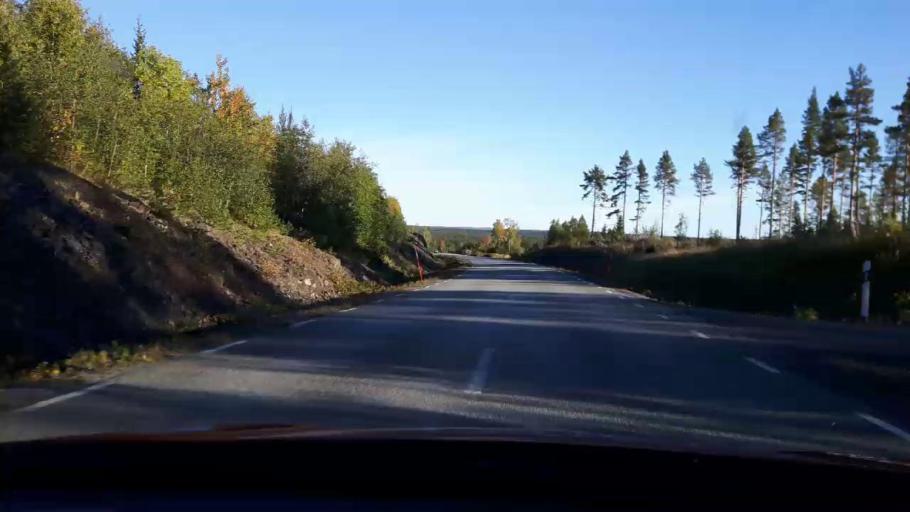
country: SE
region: Jaemtland
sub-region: OEstersunds Kommun
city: Lit
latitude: 63.7482
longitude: 14.7200
